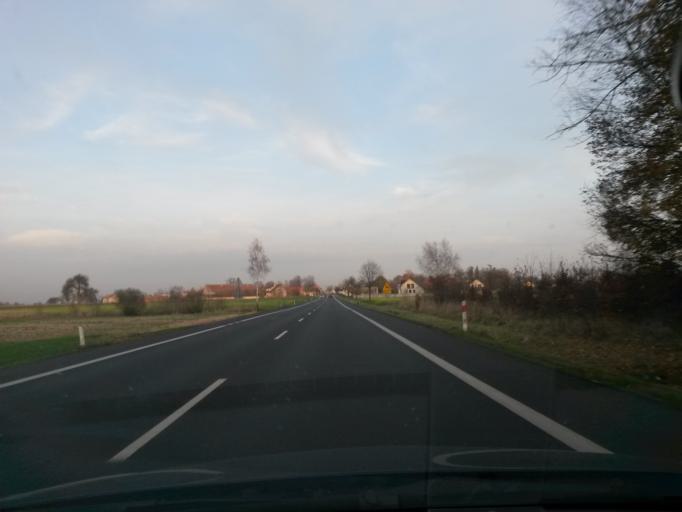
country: PL
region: Lodz Voivodeship
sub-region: Powiat wielunski
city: Osjakow
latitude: 51.2587
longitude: 18.7395
